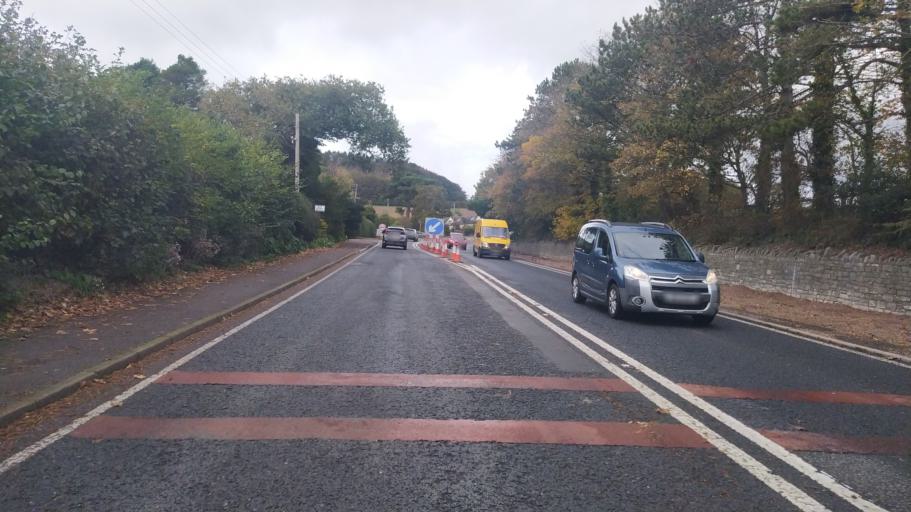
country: GB
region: England
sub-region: Dorset
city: Bridport
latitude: 50.7333
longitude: -2.8251
